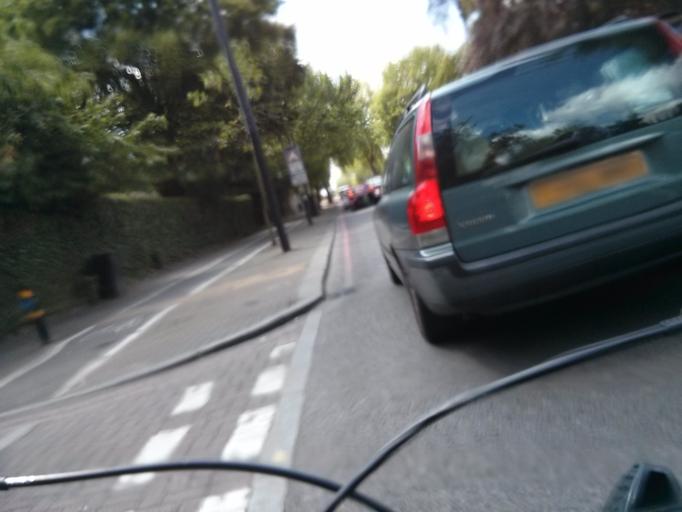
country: GB
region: England
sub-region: Greater London
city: Wandsworth
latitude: 51.4539
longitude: -0.2106
